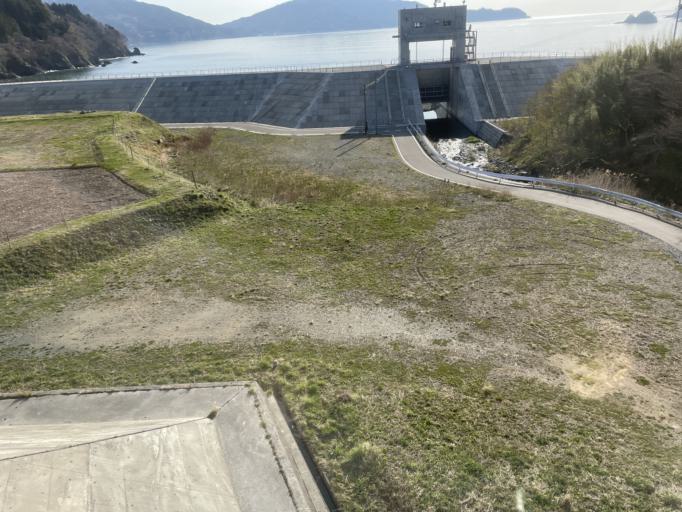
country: JP
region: Iwate
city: Ofunato
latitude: 39.0905
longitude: 141.8072
